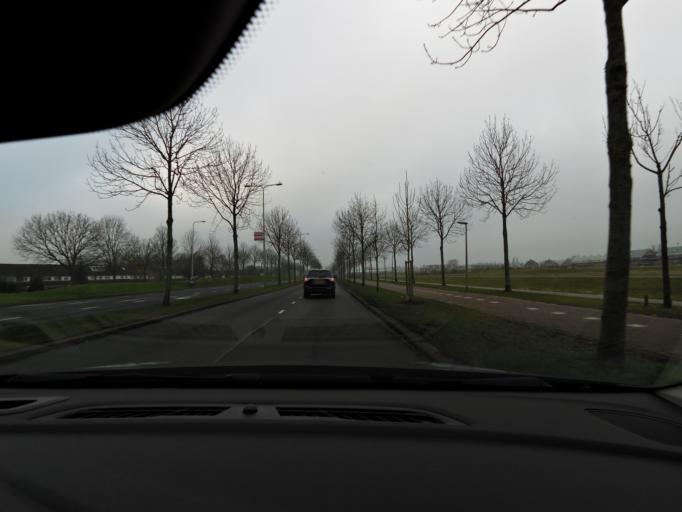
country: NL
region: South Holland
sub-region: Gemeente Spijkenisse
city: Spijkenisse
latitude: 51.8483
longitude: 4.3382
